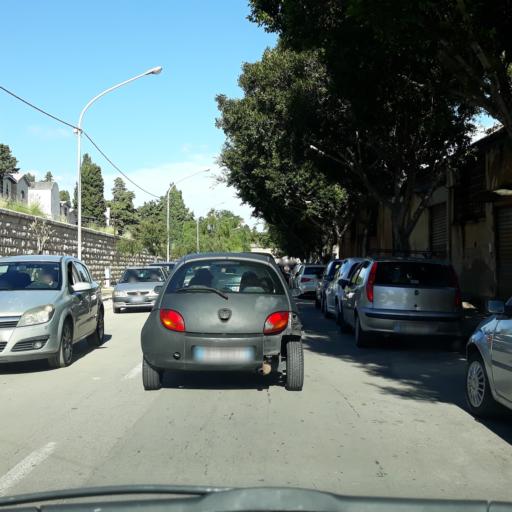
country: IT
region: Sicily
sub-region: Palermo
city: Palermo
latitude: 38.1573
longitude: 13.3709
